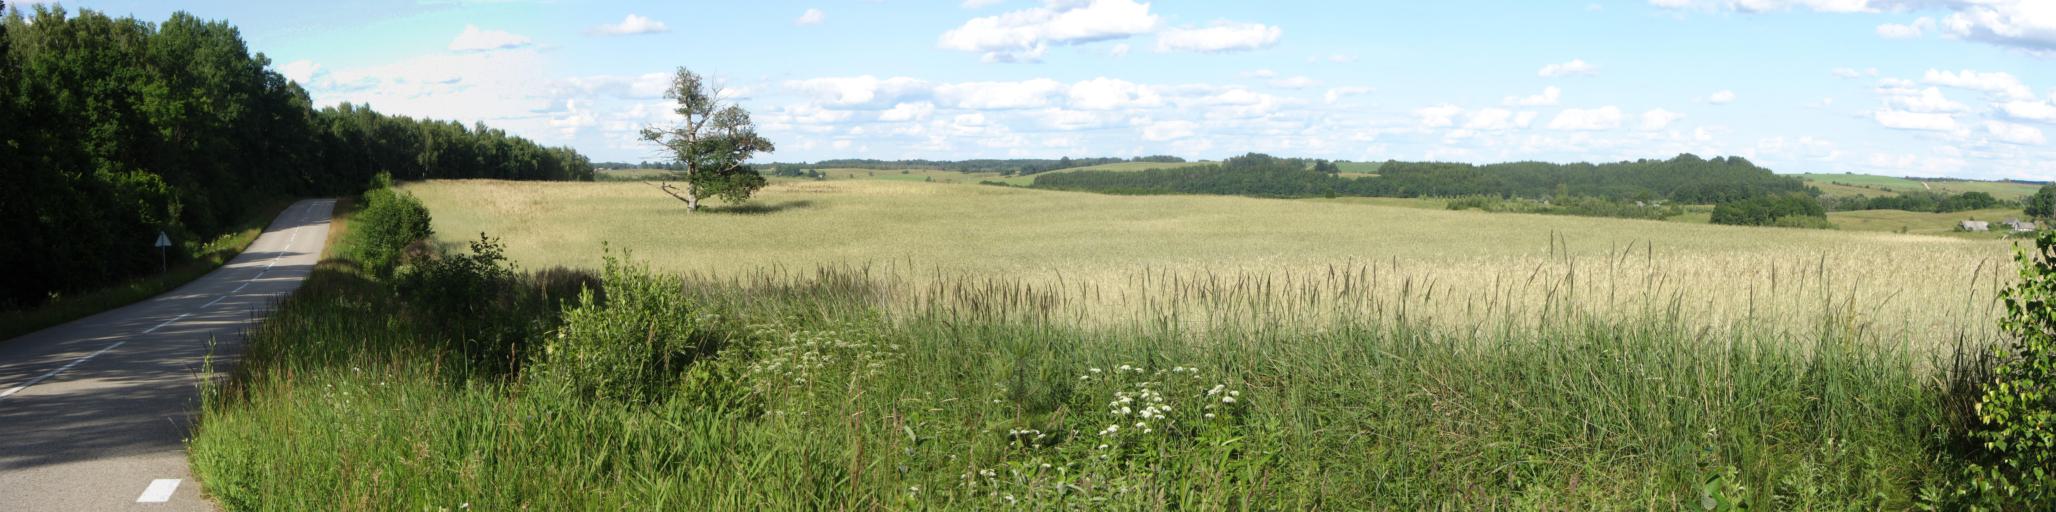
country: LT
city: Svencionys
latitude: 55.2157
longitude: 26.3165
